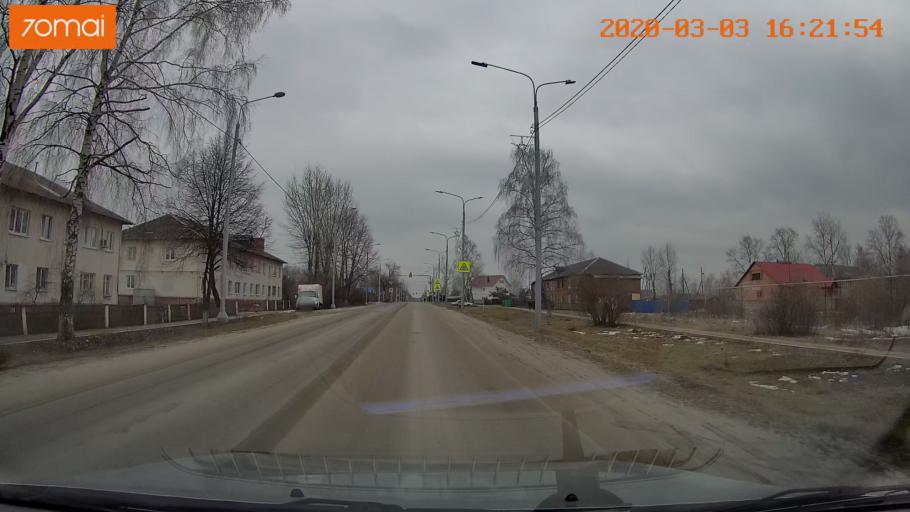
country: RU
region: Moskovskaya
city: Imeni Tsyurupy
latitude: 55.4948
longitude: 38.6463
